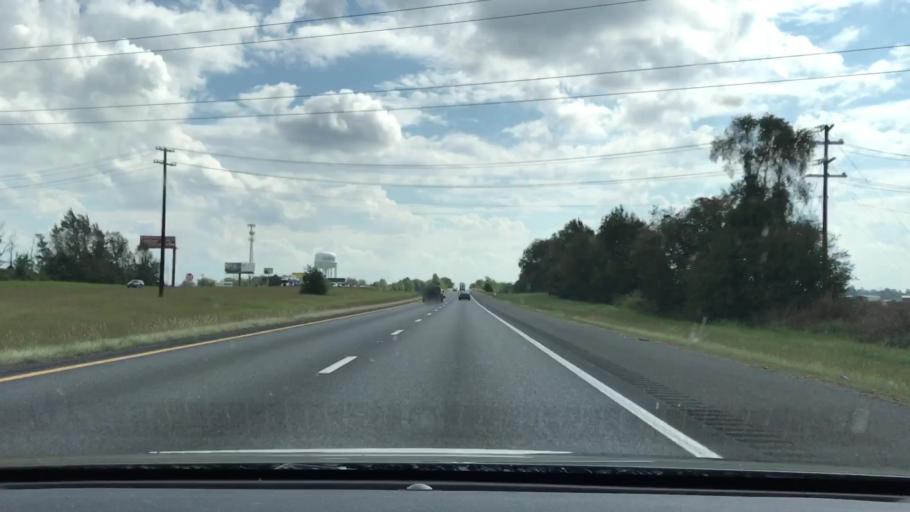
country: US
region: Tennessee
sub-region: Montgomery County
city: Clarksville
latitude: 36.5915
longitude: -87.2795
